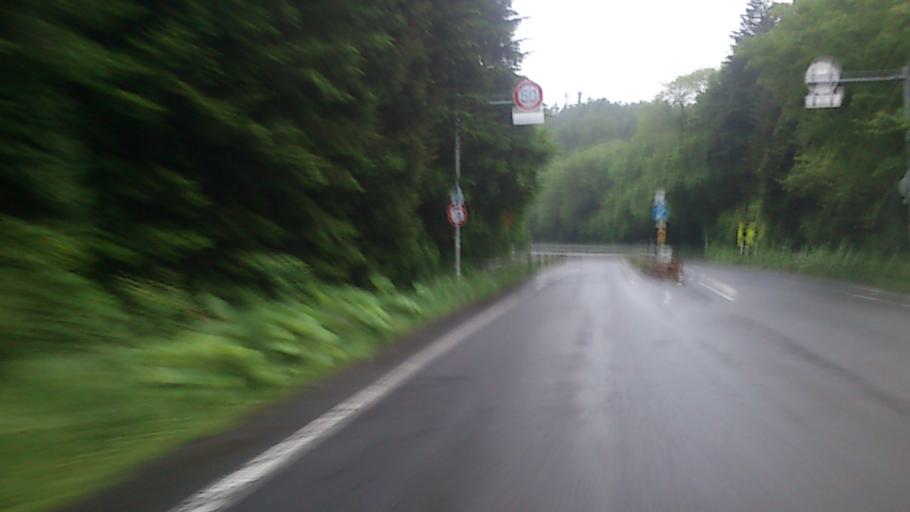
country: JP
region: Hokkaido
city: Chitose
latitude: 42.8085
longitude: 141.5869
